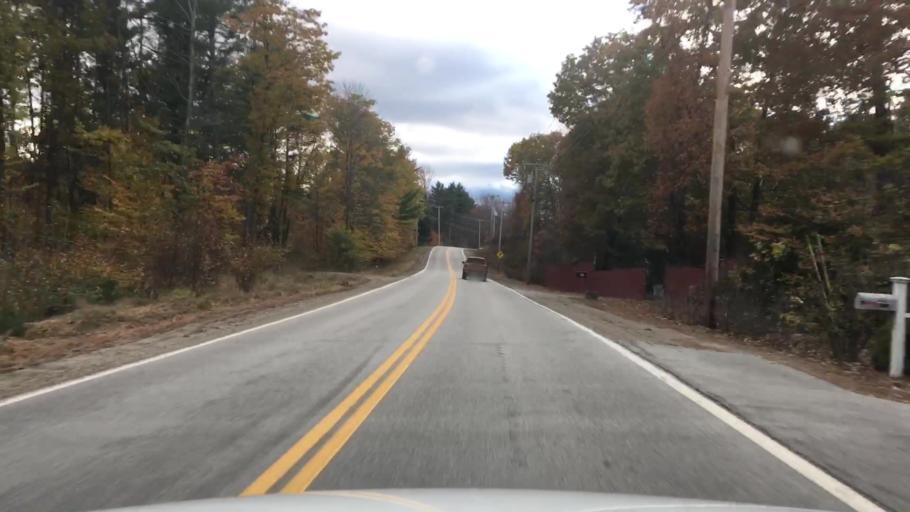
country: US
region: Maine
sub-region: Androscoggin County
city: Livermore
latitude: 44.3318
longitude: -70.2087
